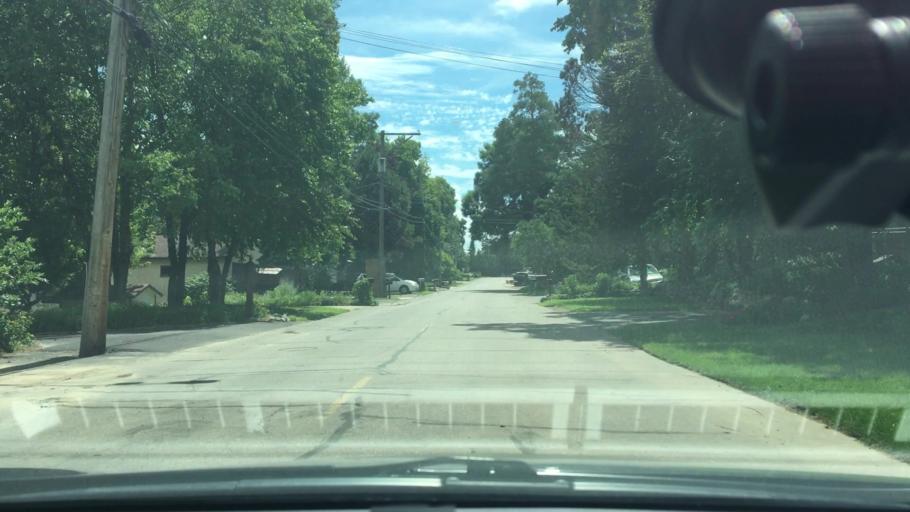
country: US
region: Minnesota
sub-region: Hennepin County
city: Plymouth
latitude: 45.0010
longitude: -93.4203
